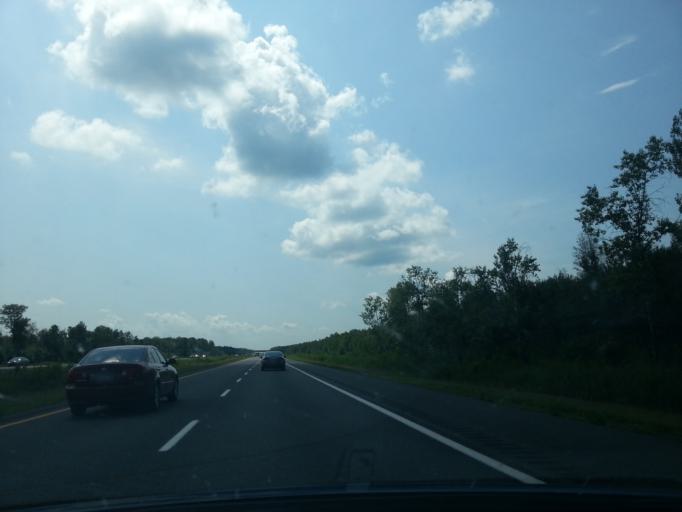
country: CA
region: Quebec
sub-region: Mauricie
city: Daveluyville
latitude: 46.1410
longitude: -72.1795
